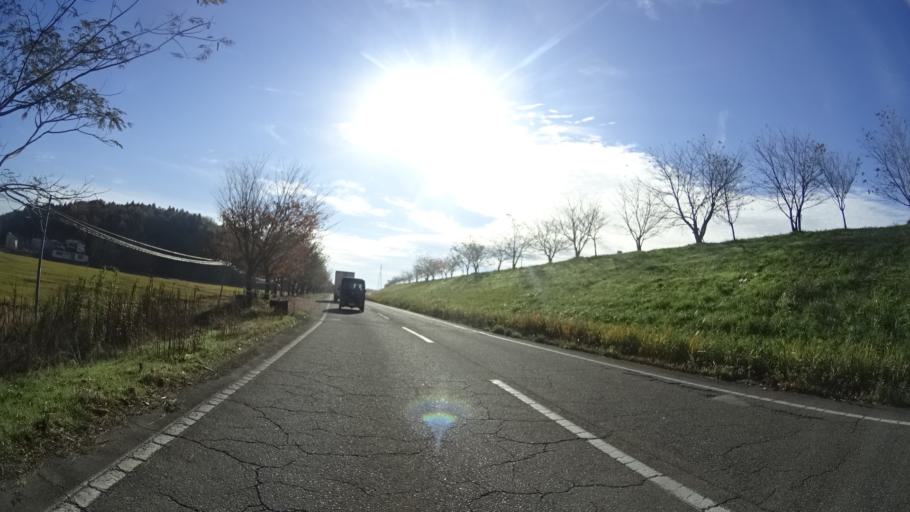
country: JP
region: Niigata
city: Yoshida-kasugacho
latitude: 37.6493
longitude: 138.8152
